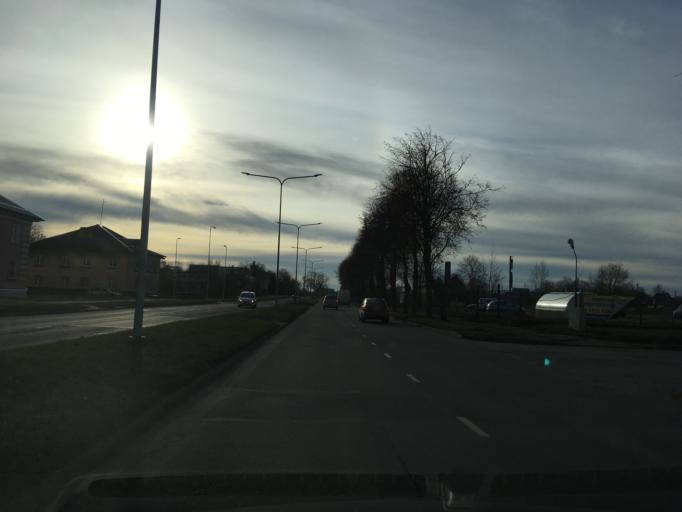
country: EE
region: Ida-Virumaa
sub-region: Narva linn
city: Narva
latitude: 59.3639
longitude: 28.1880
